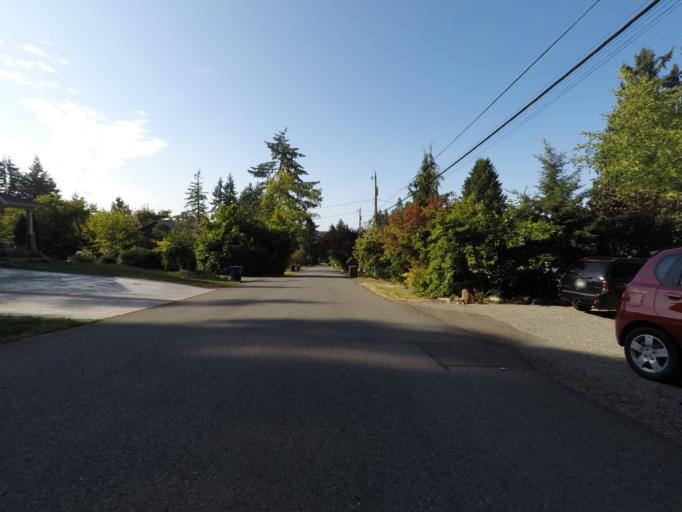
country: US
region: Washington
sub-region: King County
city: Kenmore
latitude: 47.7489
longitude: -122.2348
